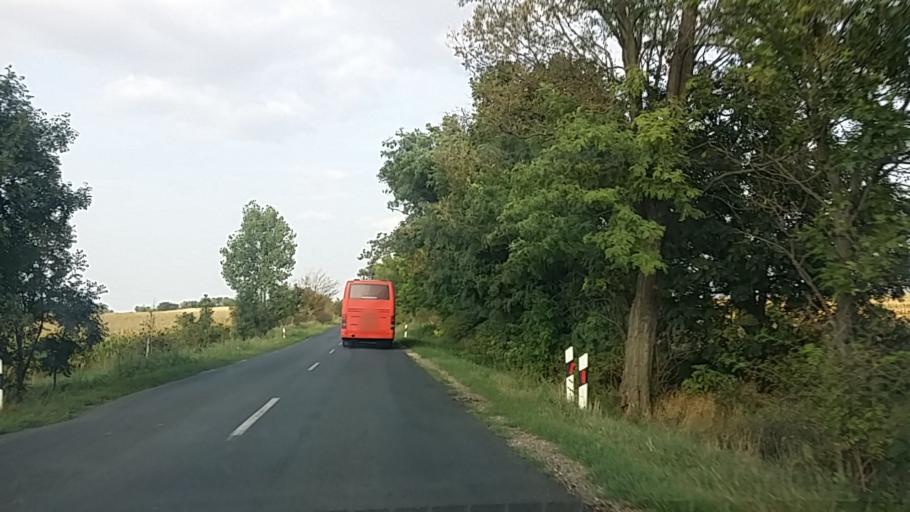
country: HU
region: Komarom-Esztergom
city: Kocs
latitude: 47.6217
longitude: 18.2382
